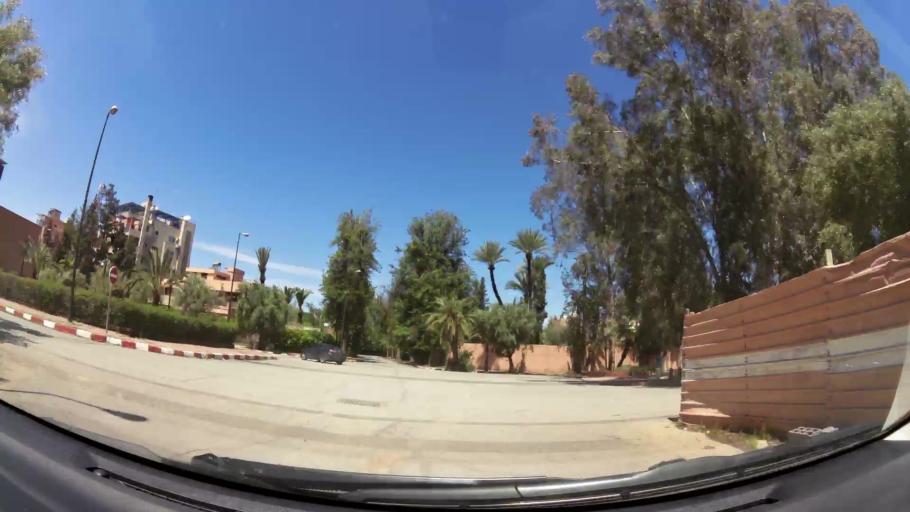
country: MA
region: Marrakech-Tensift-Al Haouz
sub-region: Marrakech
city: Marrakesh
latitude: 31.6223
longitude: -8.0092
